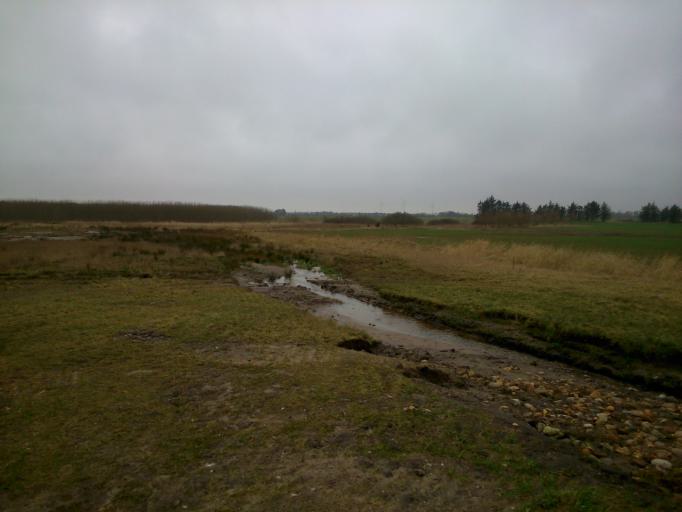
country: DK
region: Central Jutland
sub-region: Ringkobing-Skjern Kommune
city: Ringkobing
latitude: 56.1121
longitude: 8.4134
